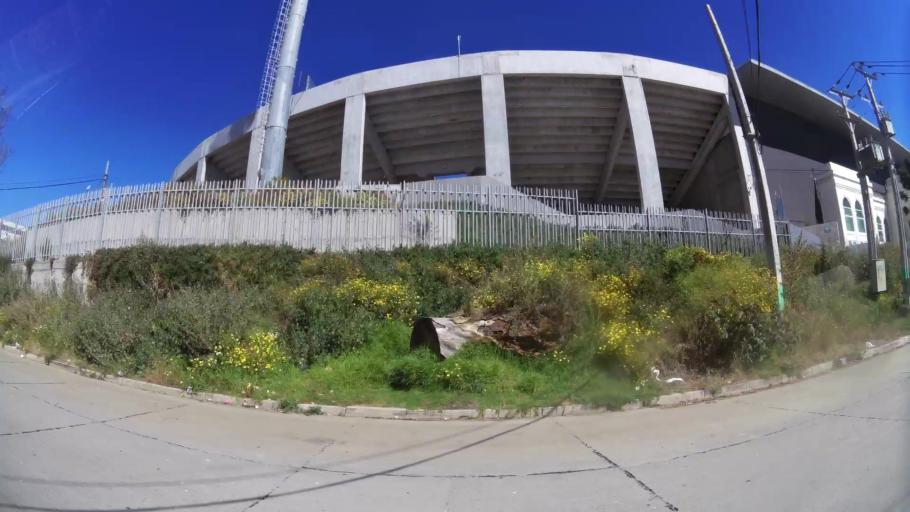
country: CL
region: Valparaiso
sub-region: Provincia de Valparaiso
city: Valparaiso
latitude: -33.0214
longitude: -71.6402
